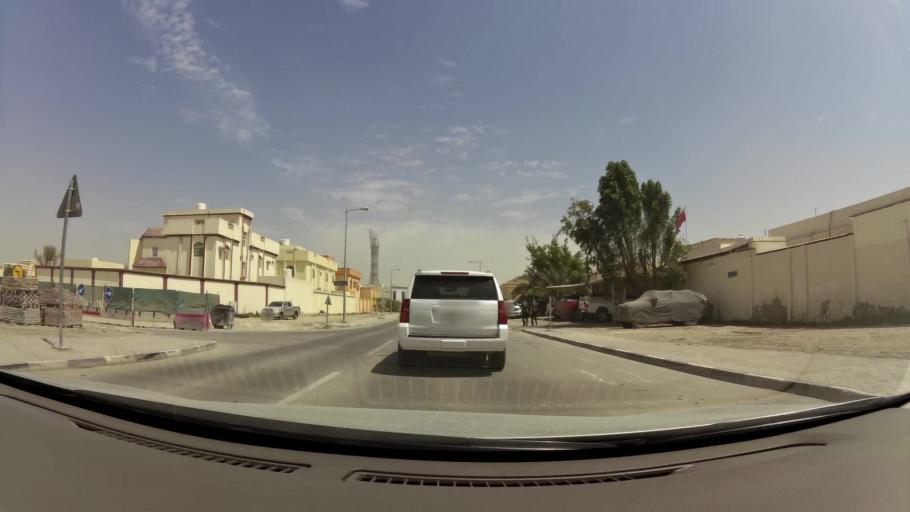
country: QA
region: Baladiyat ar Rayyan
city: Ar Rayyan
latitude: 25.2602
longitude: 51.4279
